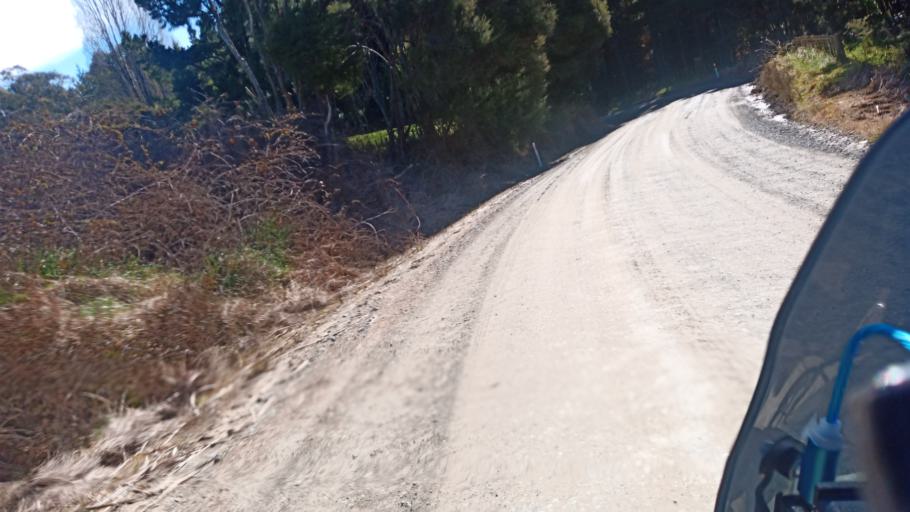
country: NZ
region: Gisborne
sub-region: Gisborne District
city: Gisborne
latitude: -37.9951
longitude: 178.3104
